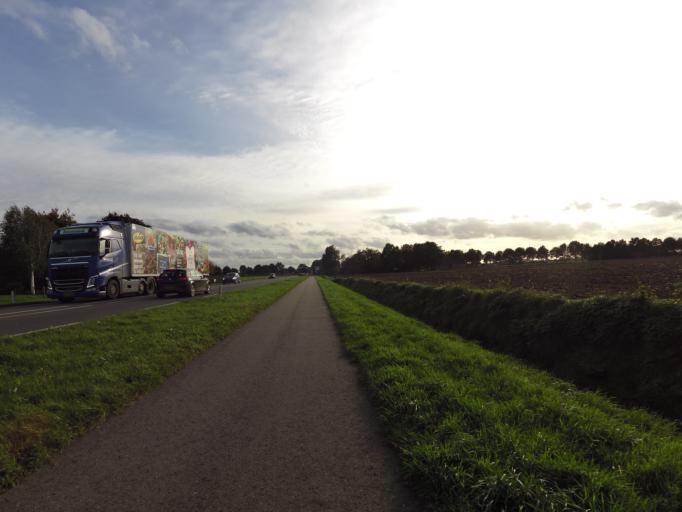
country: NL
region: Gelderland
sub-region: Gemeente Bronckhorst
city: Baak
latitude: 52.0401
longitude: 6.2177
